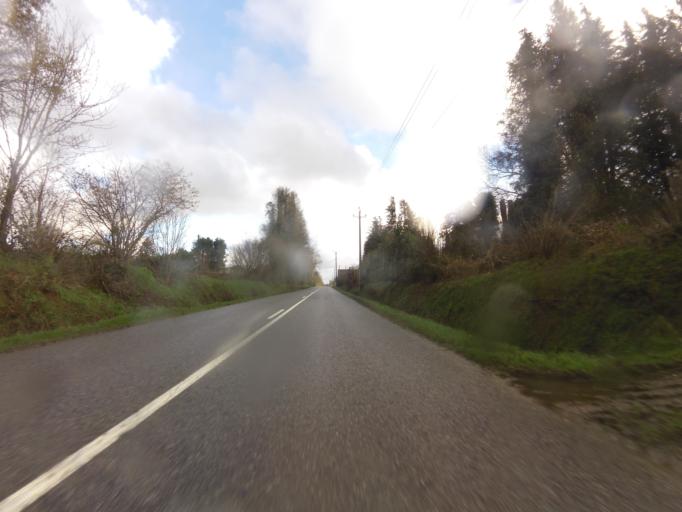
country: FR
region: Brittany
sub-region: Departement du Morbihan
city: Langonnet
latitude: 48.1435
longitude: -3.4733
